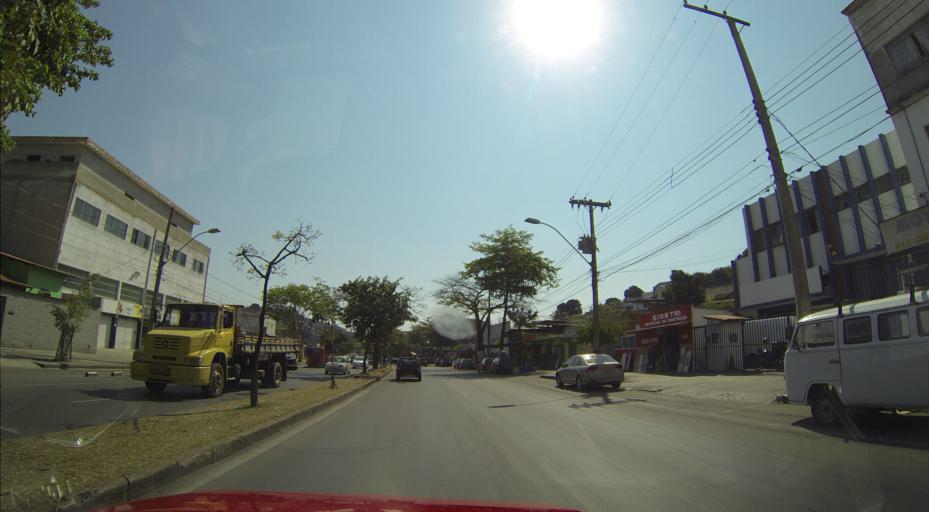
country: BR
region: Minas Gerais
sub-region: Belo Horizonte
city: Belo Horizonte
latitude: -19.8922
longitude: -43.9581
